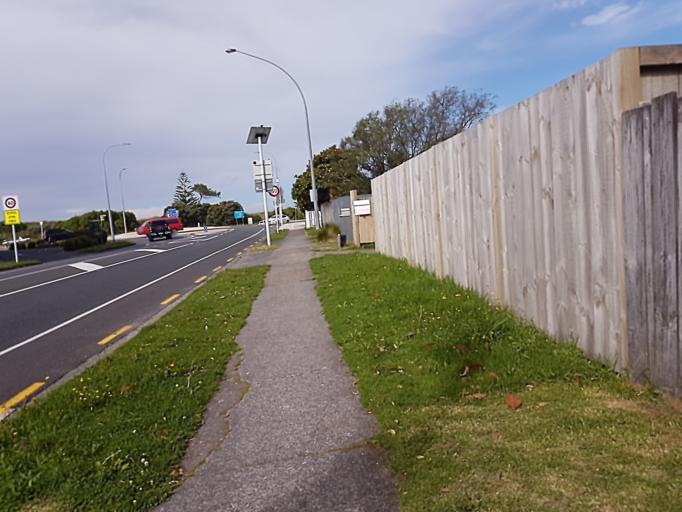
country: NZ
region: Bay of Plenty
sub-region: Western Bay of Plenty District
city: Maketu
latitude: -37.7093
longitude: 176.3168
